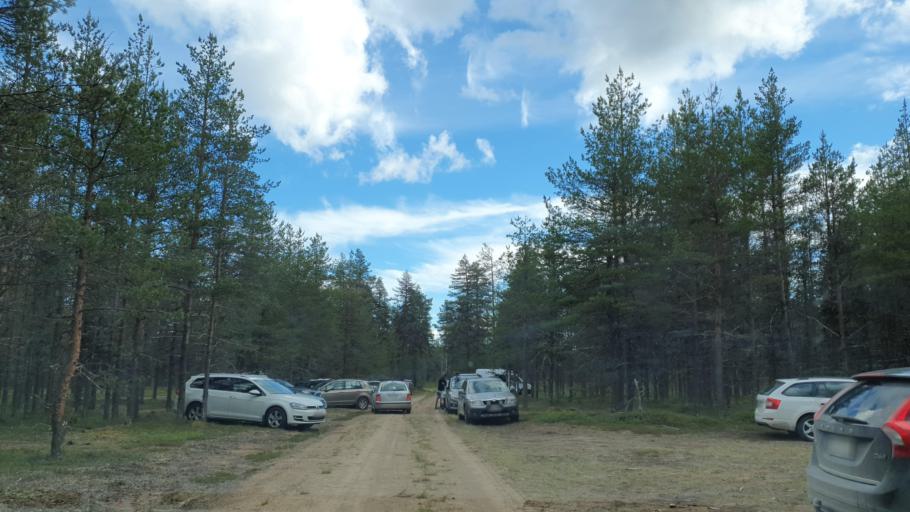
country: FI
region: Lapland
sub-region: Tunturi-Lappi
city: Kolari
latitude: 67.5399
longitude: 23.9130
